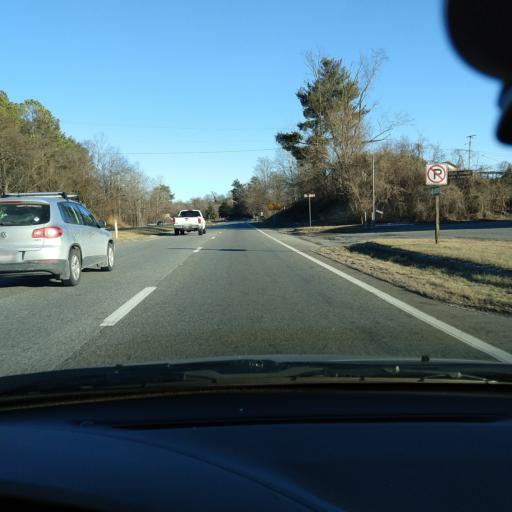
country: US
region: Virginia
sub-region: City of Bedford
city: Bedford
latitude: 37.3509
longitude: -79.6212
